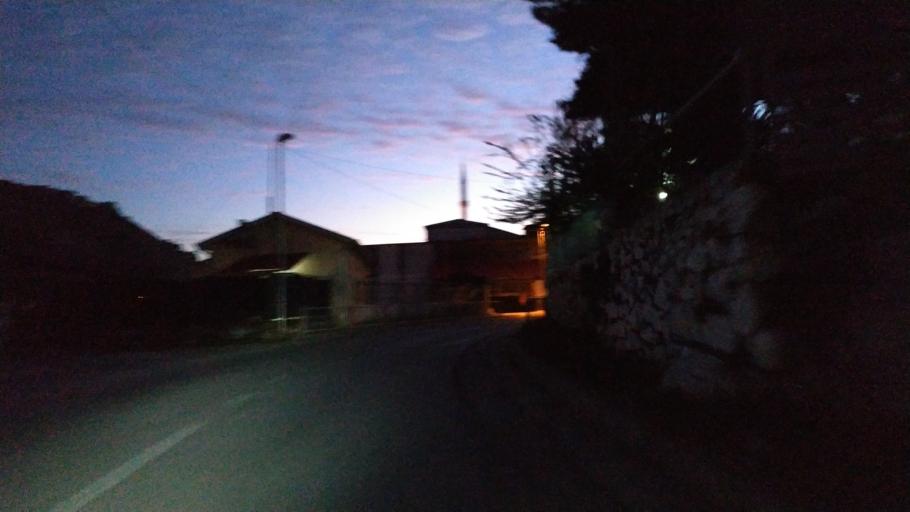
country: AL
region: Shkoder
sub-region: Rrethi i Shkodres
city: Shkoder
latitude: 42.0524
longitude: 19.4906
